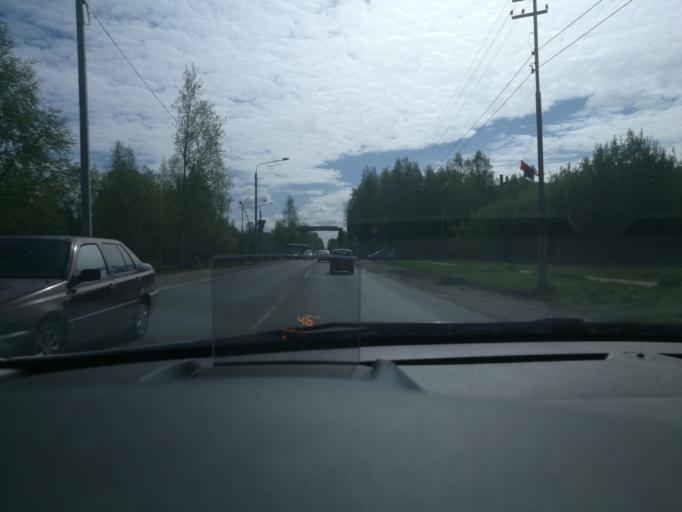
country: RU
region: Arkhangelskaya
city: Arkhangel'sk
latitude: 64.5947
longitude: 40.5773
